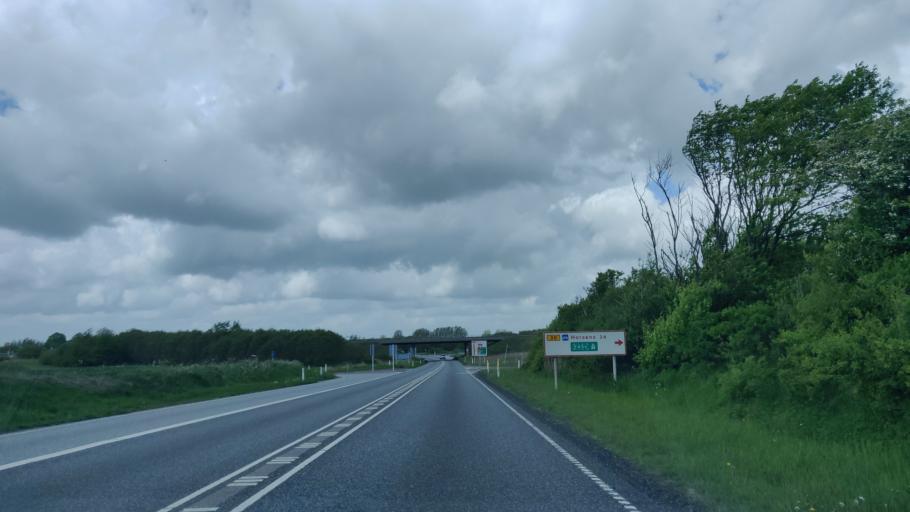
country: DK
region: Central Jutland
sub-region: Hedensted Kommune
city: Torring
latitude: 55.8363
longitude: 9.5112
